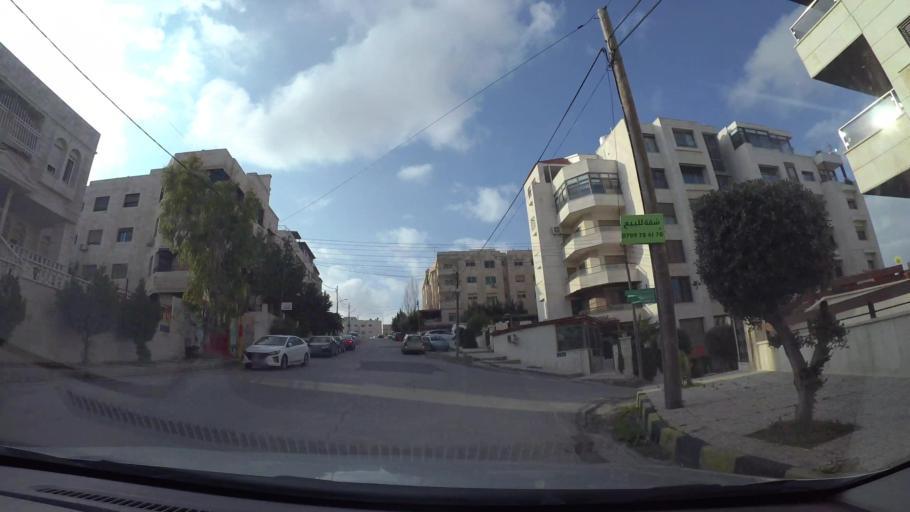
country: JO
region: Amman
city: Al Jubayhah
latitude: 31.9827
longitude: 35.8564
